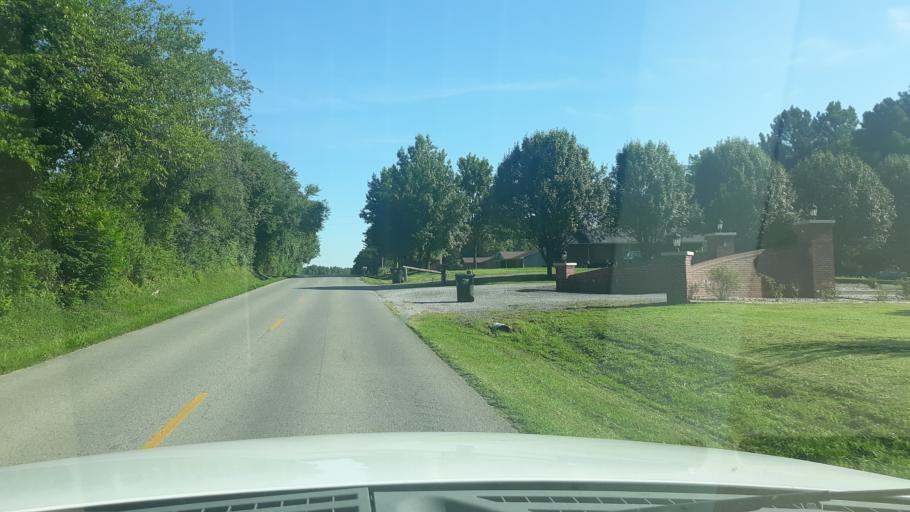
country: US
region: Illinois
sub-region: Saline County
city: Harrisburg
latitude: 37.7304
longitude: -88.5688
